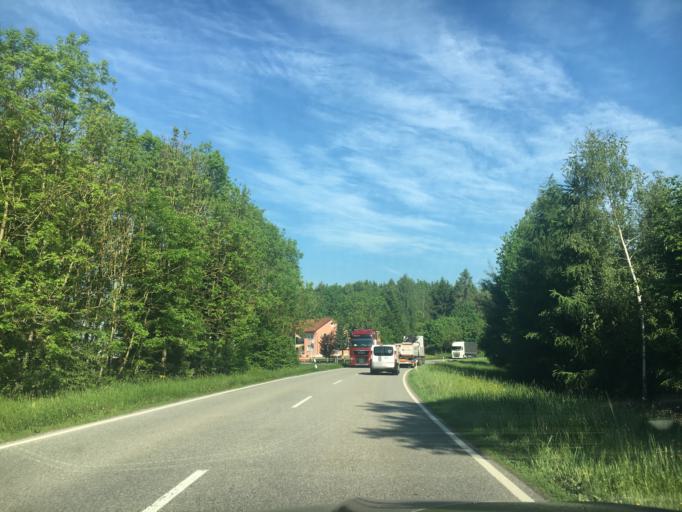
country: DE
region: Bavaria
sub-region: Upper Bavaria
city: Niedertaufkirchen
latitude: 48.3267
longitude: 12.5319
